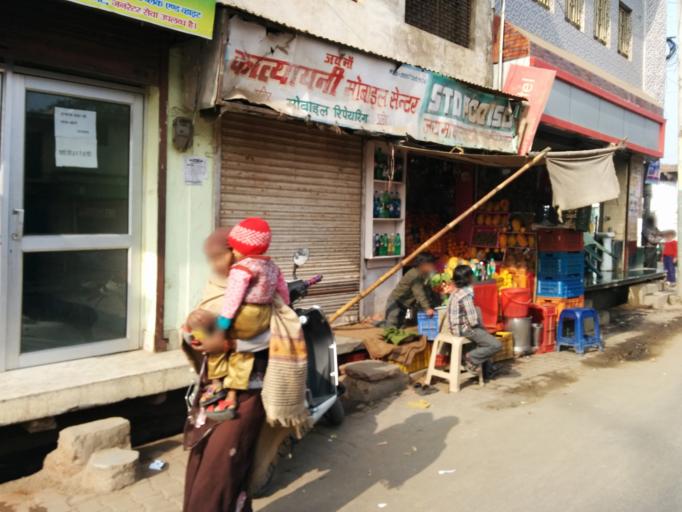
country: IN
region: Uttar Pradesh
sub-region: Mathura
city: Vrindavan
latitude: 27.5797
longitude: 77.6999
